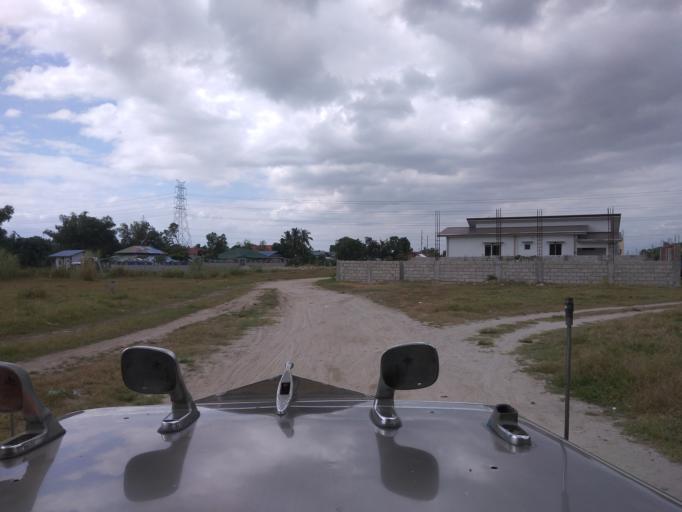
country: PH
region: Central Luzon
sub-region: Province of Pampanga
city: Anao
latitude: 15.1152
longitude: 120.7005
